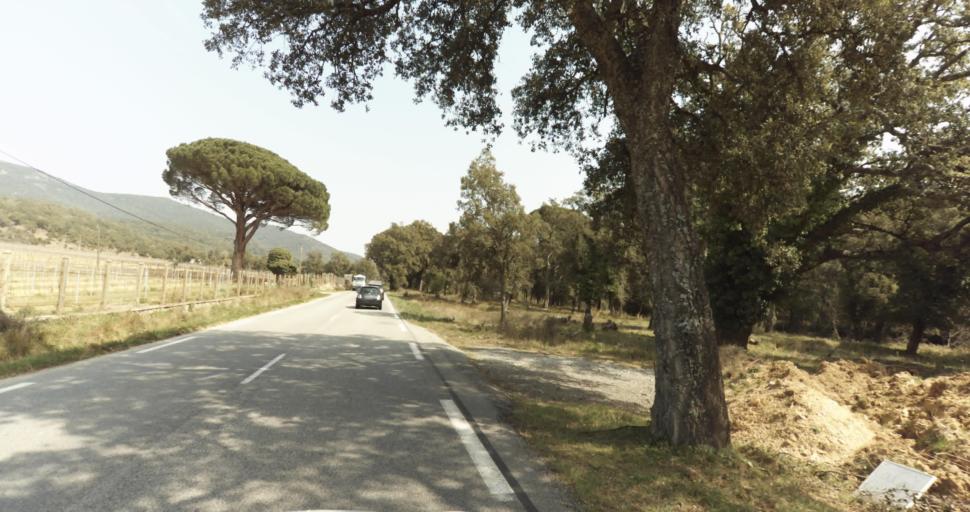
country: FR
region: Provence-Alpes-Cote d'Azur
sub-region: Departement du Var
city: Le Lavandou
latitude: 43.1972
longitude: 6.3882
